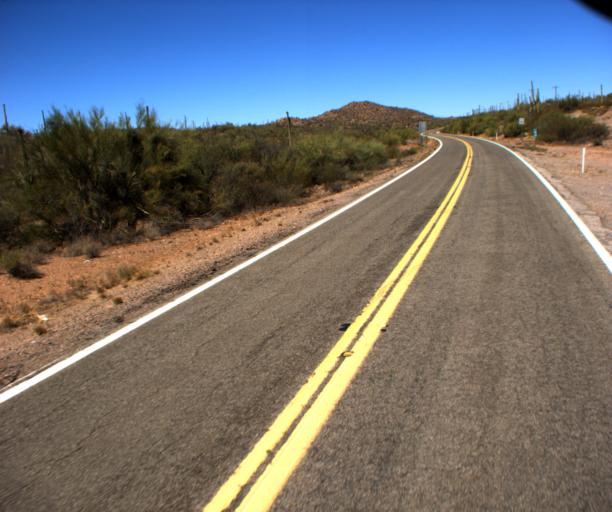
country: US
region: Arizona
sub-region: Pima County
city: Sells
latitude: 32.1750
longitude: -112.1618
